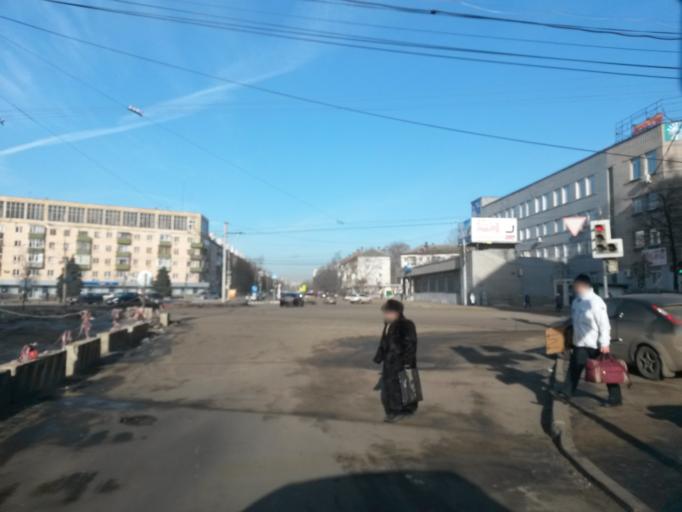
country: RU
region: Jaroslavl
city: Yaroslavl
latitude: 57.6289
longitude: 39.8496
